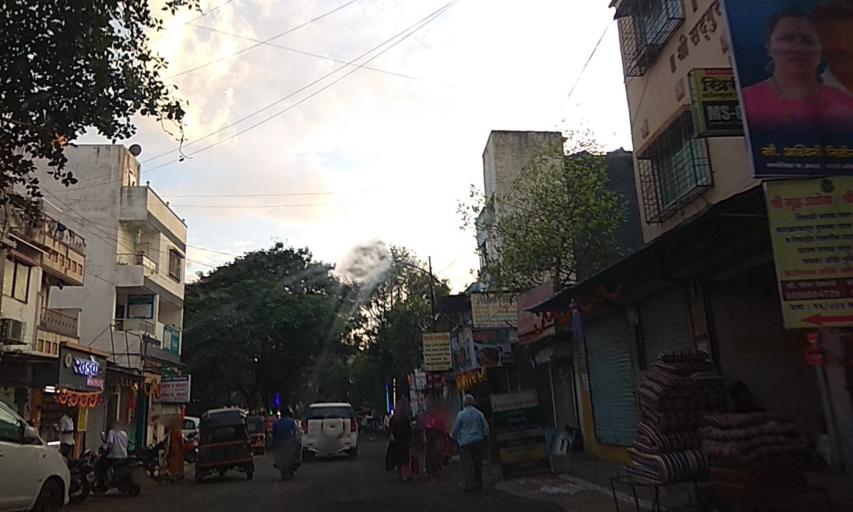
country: IN
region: Maharashtra
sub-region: Pune Division
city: Pune
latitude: 18.4935
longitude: 73.8502
